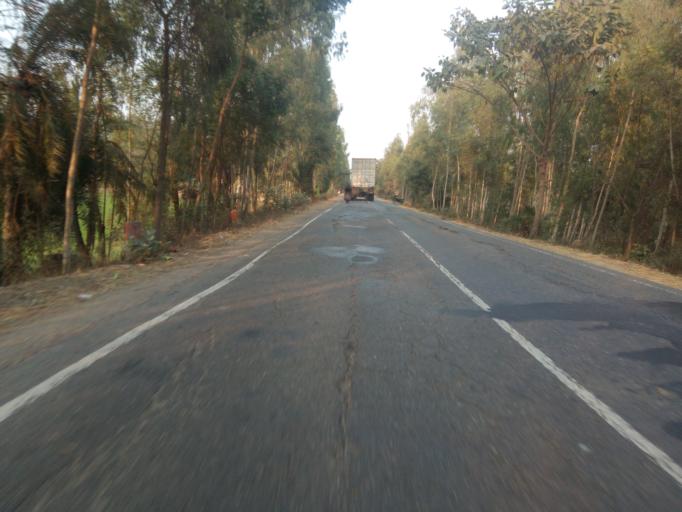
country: BD
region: Rajshahi
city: Par Naogaon
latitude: 24.5434
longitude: 89.1863
